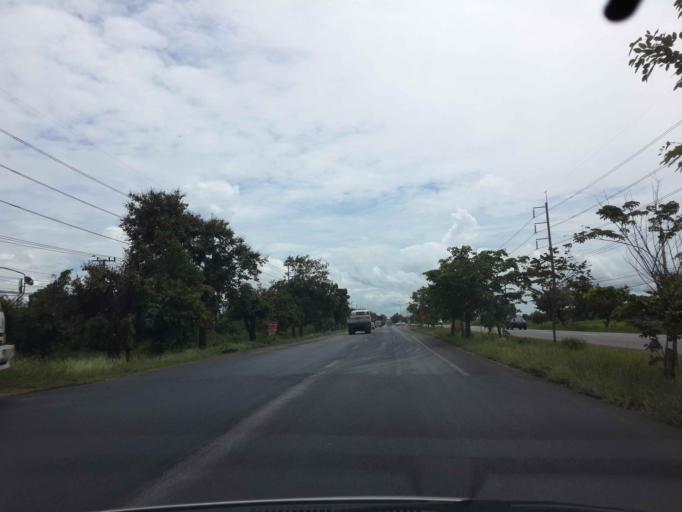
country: TH
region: Ratchaburi
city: Pak Tho
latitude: 13.4223
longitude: 99.8086
